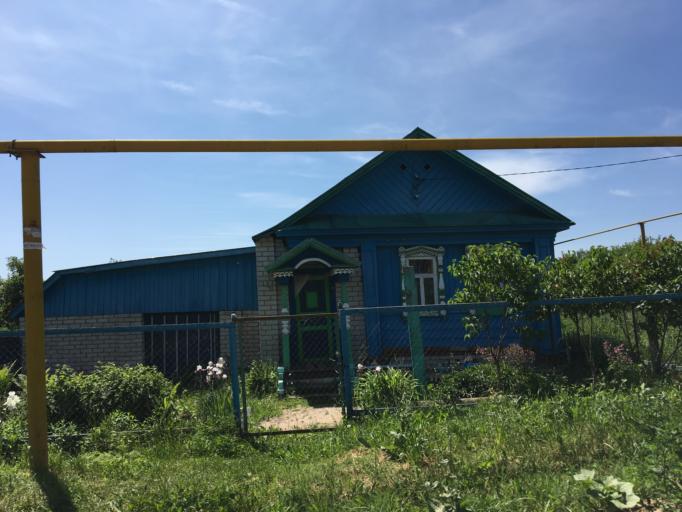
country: RU
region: Nizjnij Novgorod
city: Spasskoye
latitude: 56.1077
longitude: 45.5011
